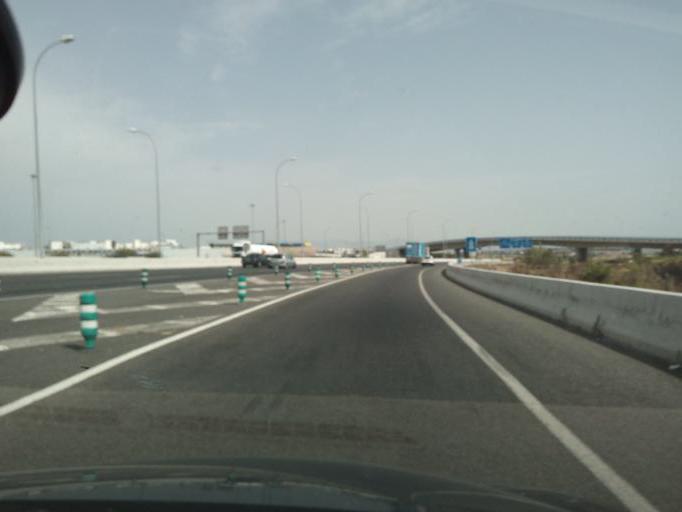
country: ES
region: Madrid
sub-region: Provincia de Madrid
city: Hortaleza
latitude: 40.4821
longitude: -3.6436
